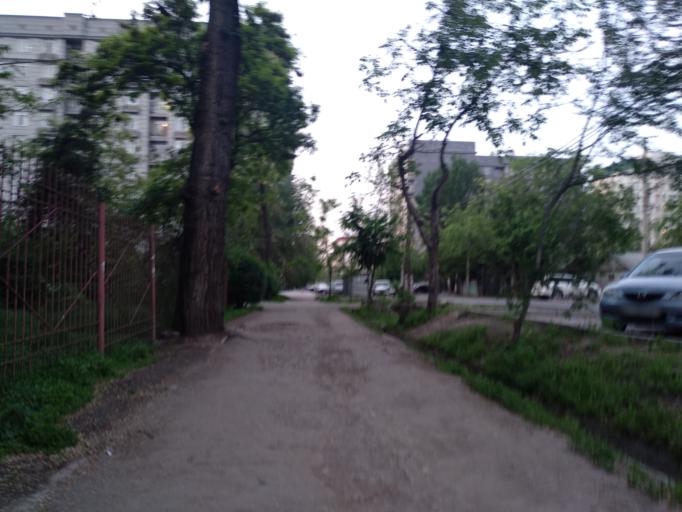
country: KG
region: Chuy
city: Bishkek
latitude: 42.8779
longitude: 74.5814
